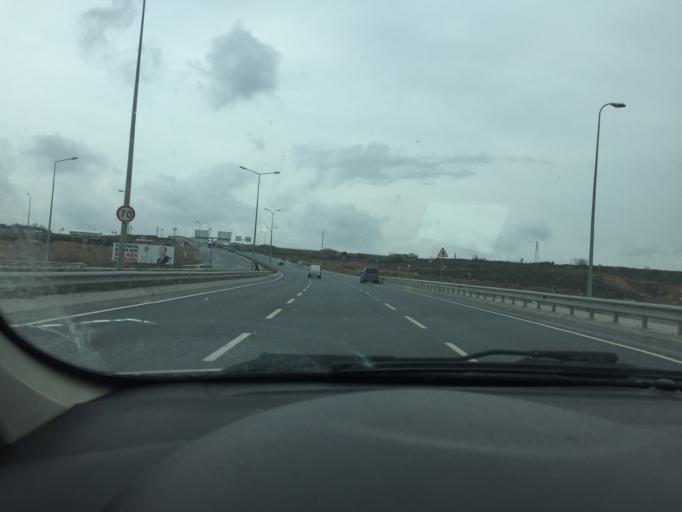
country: TR
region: Istanbul
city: Basaksehir
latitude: 41.1393
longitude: 28.7943
